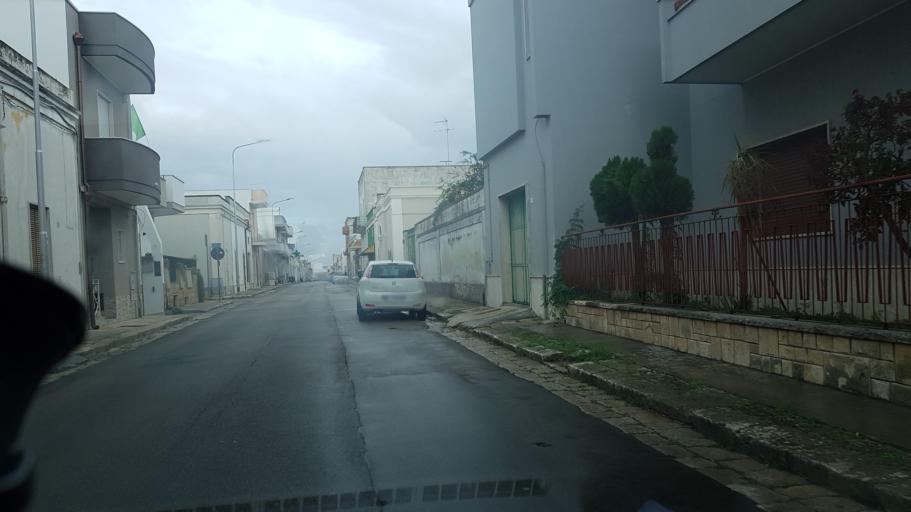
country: IT
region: Apulia
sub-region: Provincia di Lecce
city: Carmiano
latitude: 40.3451
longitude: 18.0422
